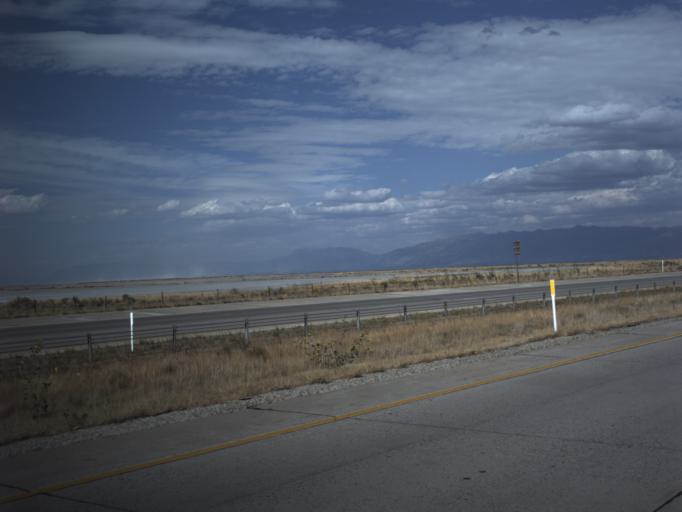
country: US
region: Utah
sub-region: Salt Lake County
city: Magna
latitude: 40.7699
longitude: -112.1518
